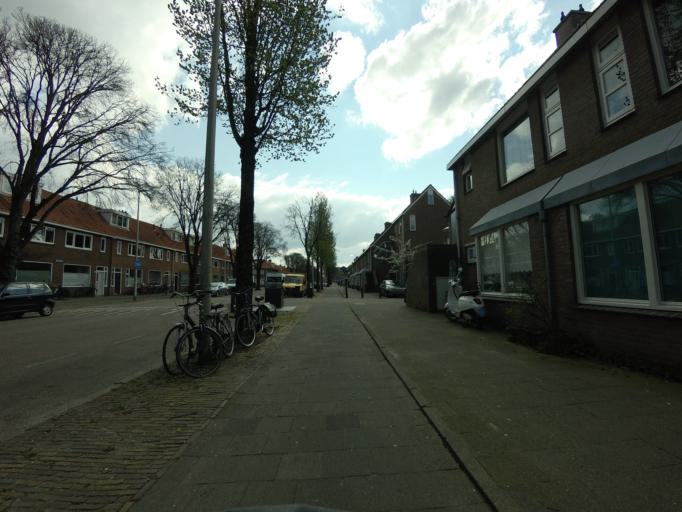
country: NL
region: Utrecht
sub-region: Gemeente Utrecht
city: Utrecht
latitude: 52.0740
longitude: 5.1160
